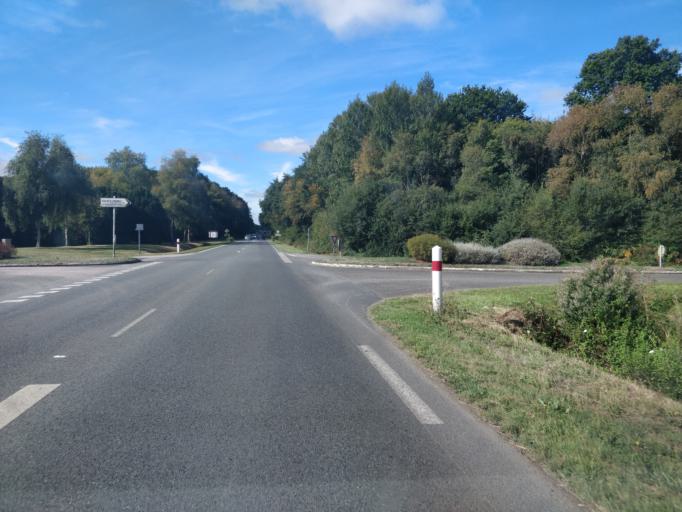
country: FR
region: Brittany
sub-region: Departement des Cotes-d'Armor
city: Erquy
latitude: 48.5956
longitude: -2.4788
